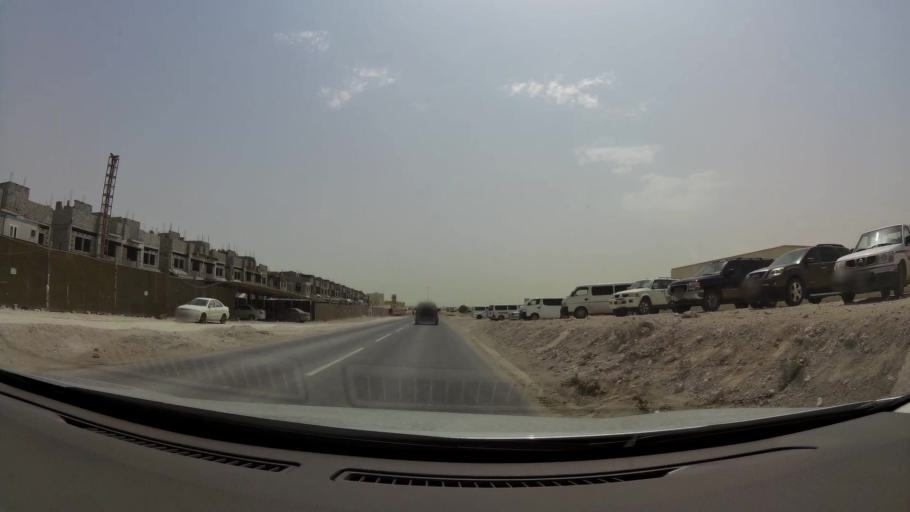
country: QA
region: Baladiyat ar Rayyan
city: Ar Rayyan
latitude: 25.2305
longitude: 51.4089
